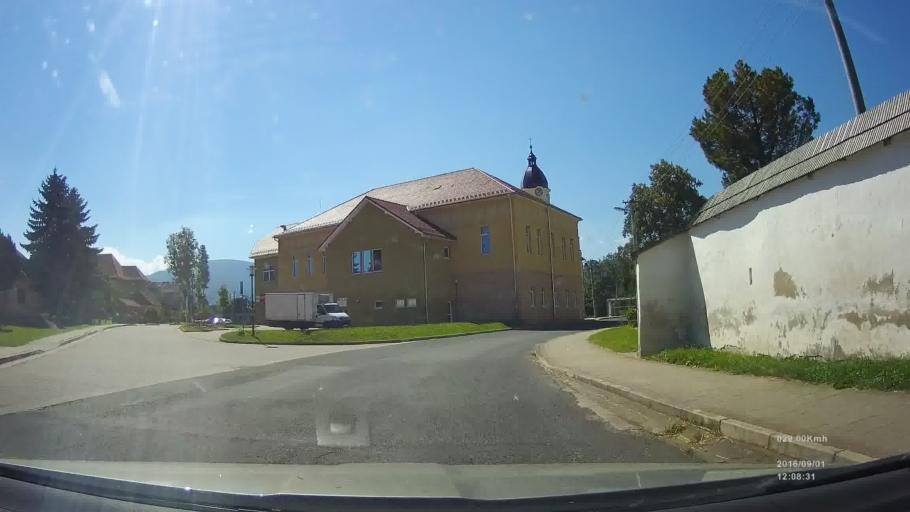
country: SK
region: Zilinsky
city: Ruzomberok
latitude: 49.0653
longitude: 19.4365
